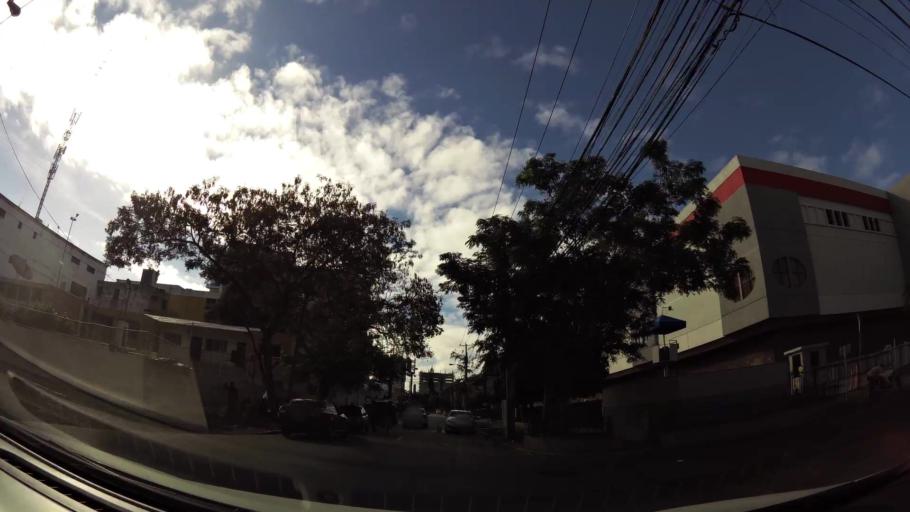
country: DO
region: Nacional
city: La Julia
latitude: 18.4653
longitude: -69.9351
